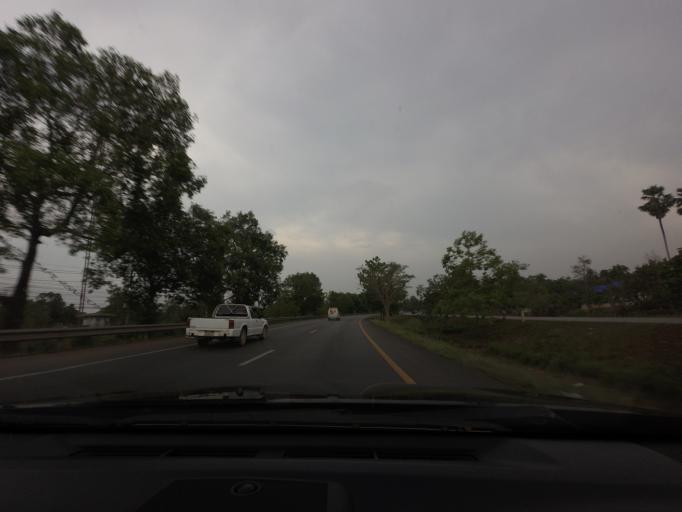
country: TH
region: Surat Thani
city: Chaiya
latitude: 9.4656
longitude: 99.1529
